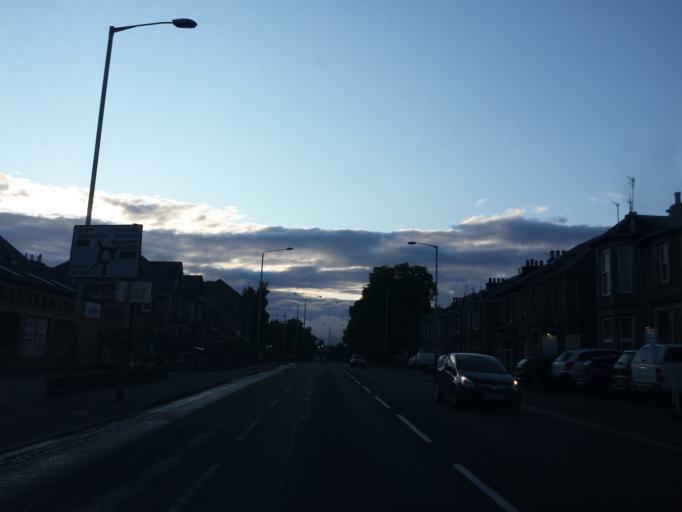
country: GB
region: Scotland
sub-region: Perth and Kinross
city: Perth
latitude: 56.4027
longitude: -3.4413
